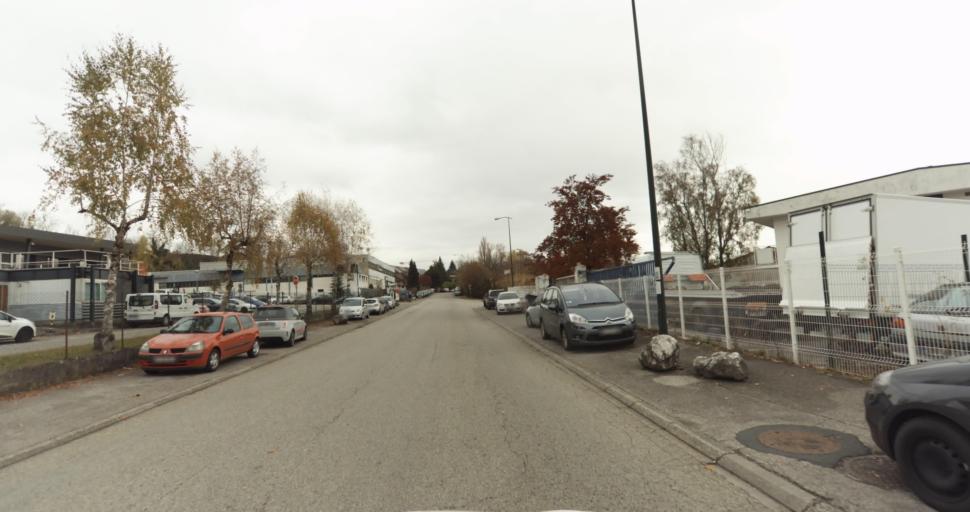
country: FR
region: Rhone-Alpes
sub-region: Departement de la Haute-Savoie
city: Annecy
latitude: 45.8842
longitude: 6.1122
